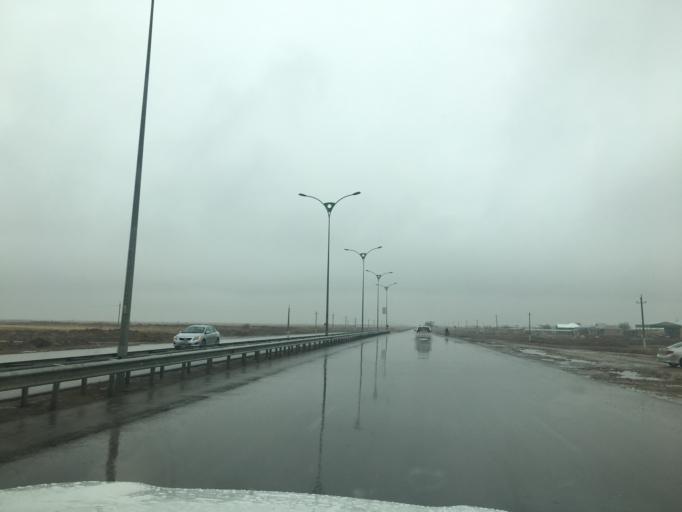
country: TM
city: Murgab
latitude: 37.4864
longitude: 61.9912
